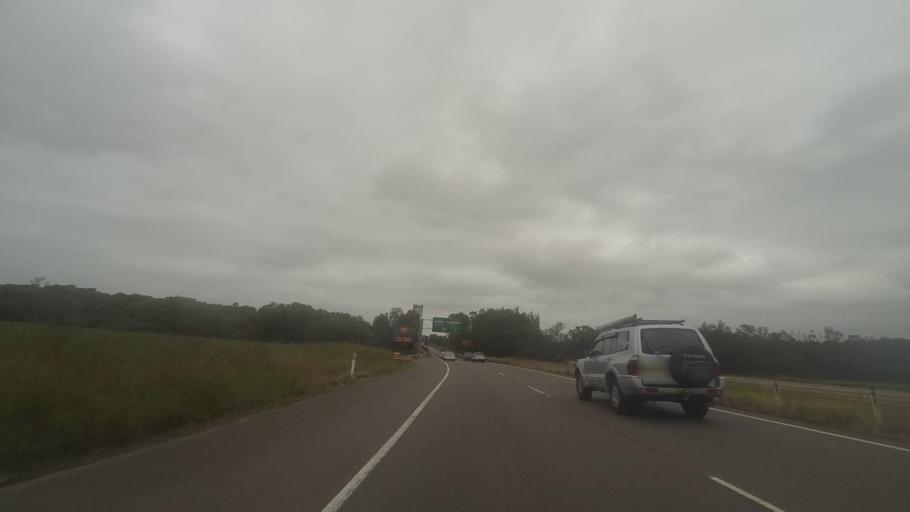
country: AU
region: New South Wales
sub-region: Newcastle
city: Beresfield
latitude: -32.8207
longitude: 151.6881
